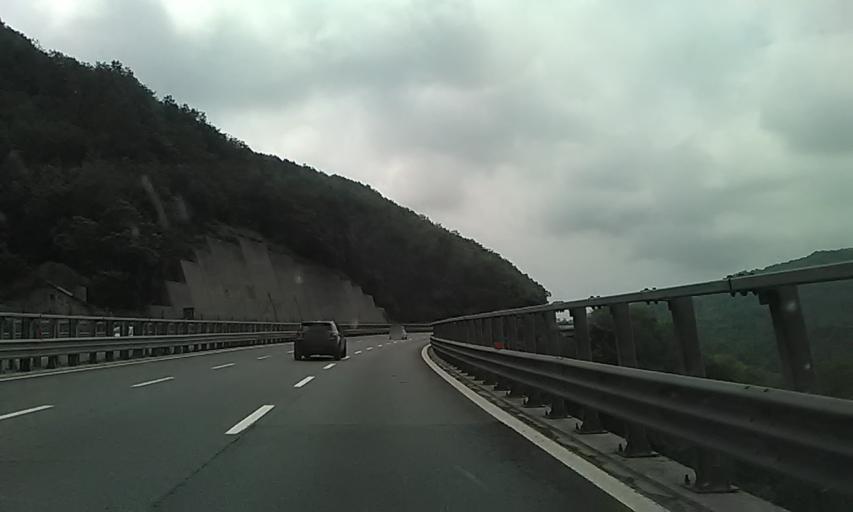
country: IT
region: Liguria
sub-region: Provincia di Genova
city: Masone
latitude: 44.4794
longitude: 8.7351
